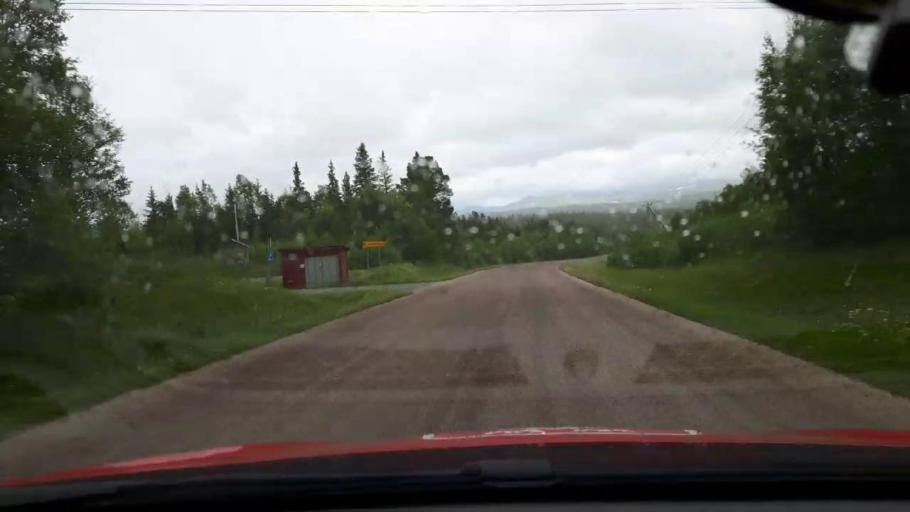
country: NO
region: Nord-Trondelag
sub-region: Meraker
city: Meraker
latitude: 63.2851
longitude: 12.3484
